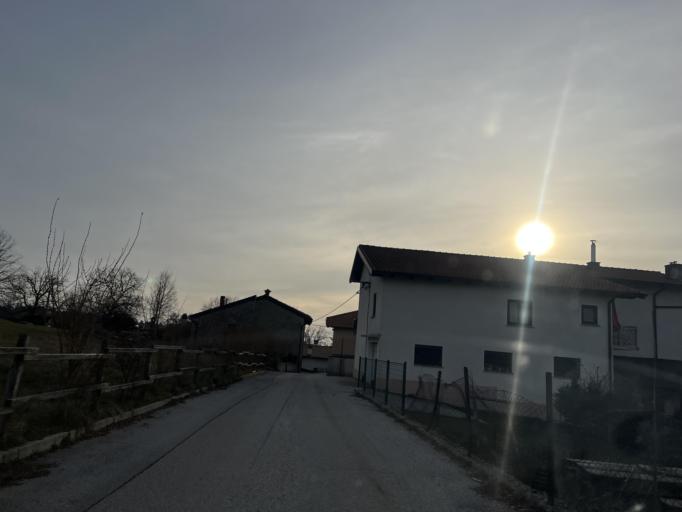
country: SI
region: Nova Gorica
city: Sempas
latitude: 45.9731
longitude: 13.7392
